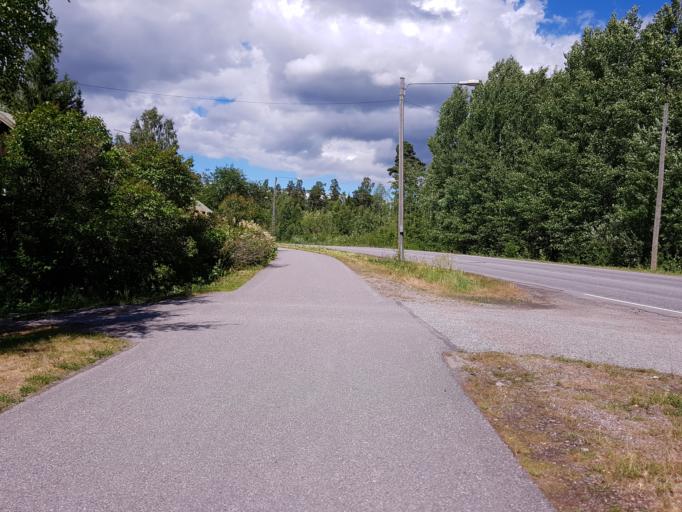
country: FI
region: Uusimaa
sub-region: Helsinki
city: Kilo
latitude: 60.3233
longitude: 24.8689
